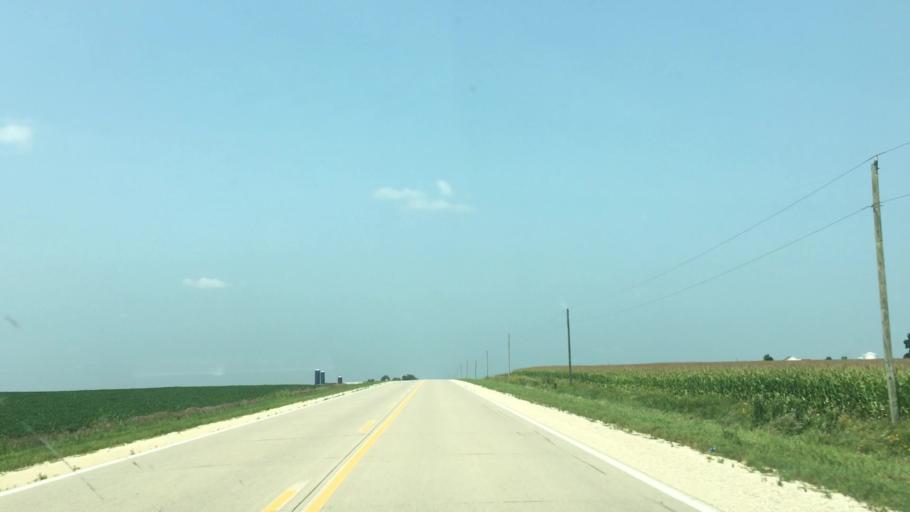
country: US
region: Iowa
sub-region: Fayette County
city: Fayette
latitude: 42.7315
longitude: -91.8040
